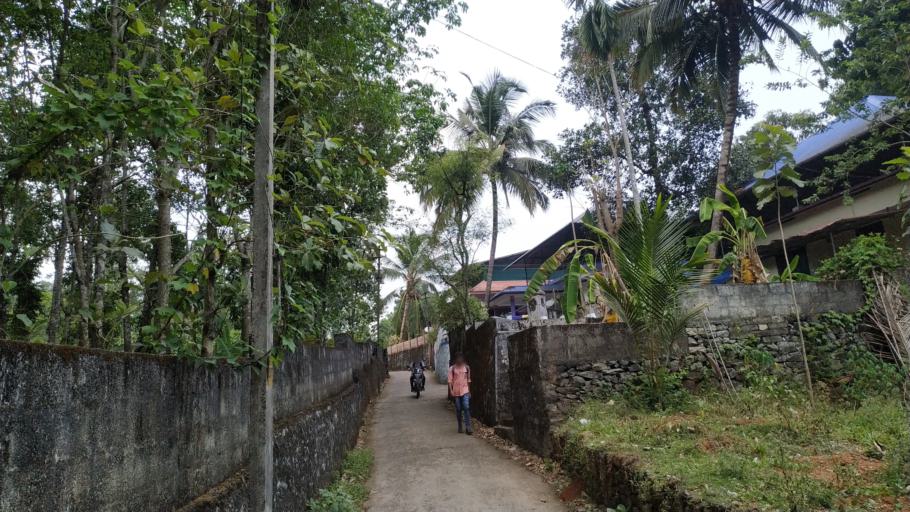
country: IN
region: Kerala
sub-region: Kottayam
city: Lalam
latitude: 9.8425
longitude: 76.7456
